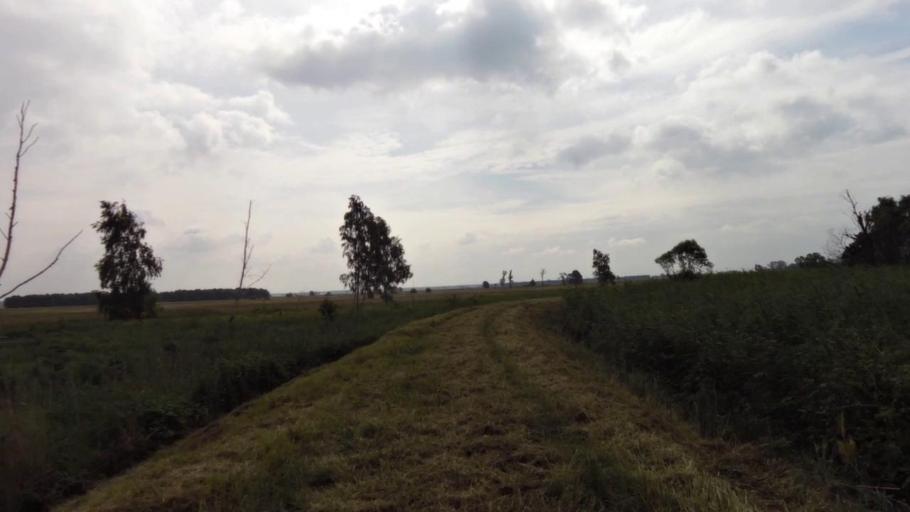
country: PL
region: West Pomeranian Voivodeship
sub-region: Powiat policki
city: Police
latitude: 53.5367
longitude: 14.6778
